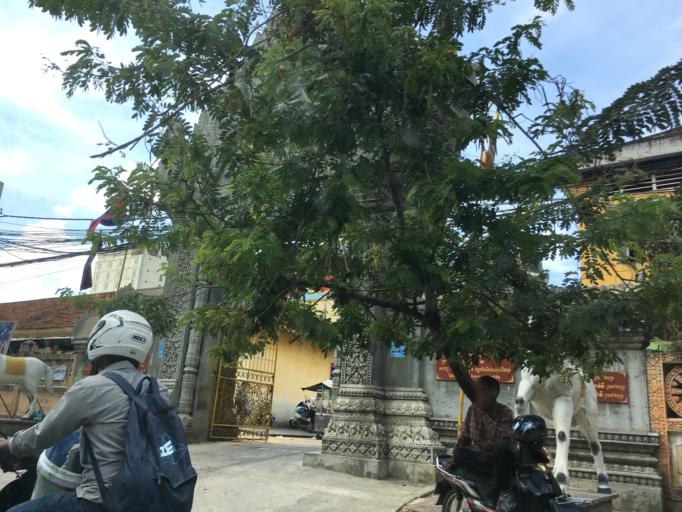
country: KH
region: Phnom Penh
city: Phnom Penh
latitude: 11.5439
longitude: 104.9156
